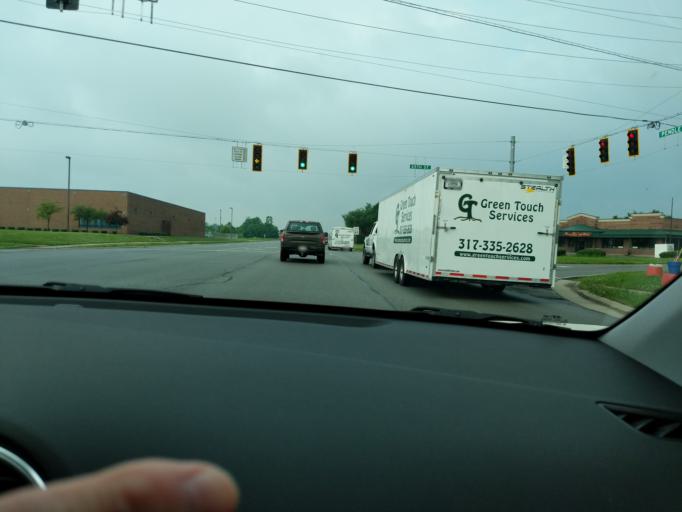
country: US
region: Indiana
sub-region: Hancock County
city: McCordsville
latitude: 39.8771
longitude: -85.9516
